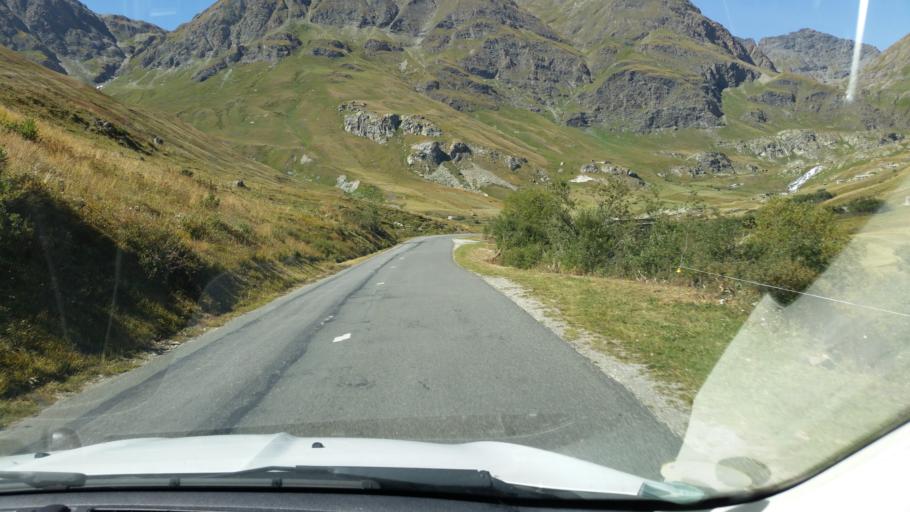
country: FR
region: Rhone-Alpes
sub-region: Departement de la Savoie
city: Val-d'Isere
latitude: 45.3838
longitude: 7.0438
